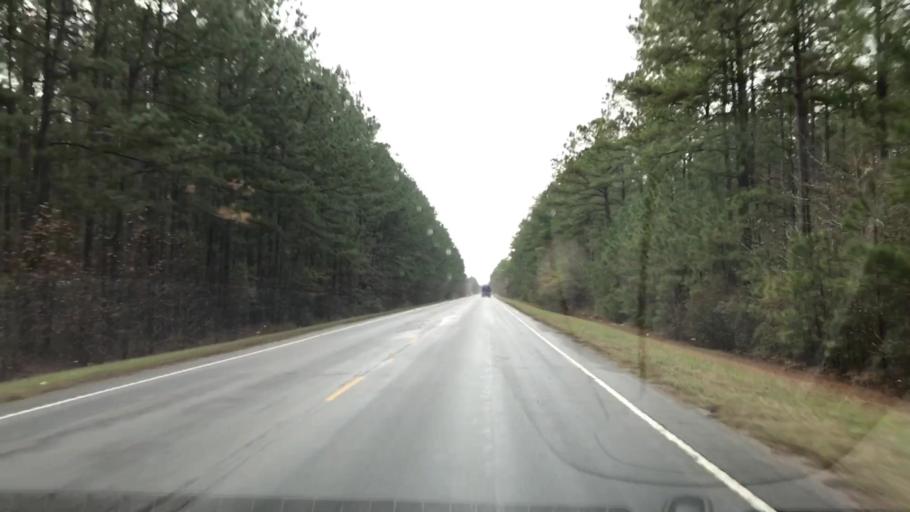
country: US
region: South Carolina
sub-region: Berkeley County
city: Saint Stephen
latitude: 33.2869
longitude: -79.8477
